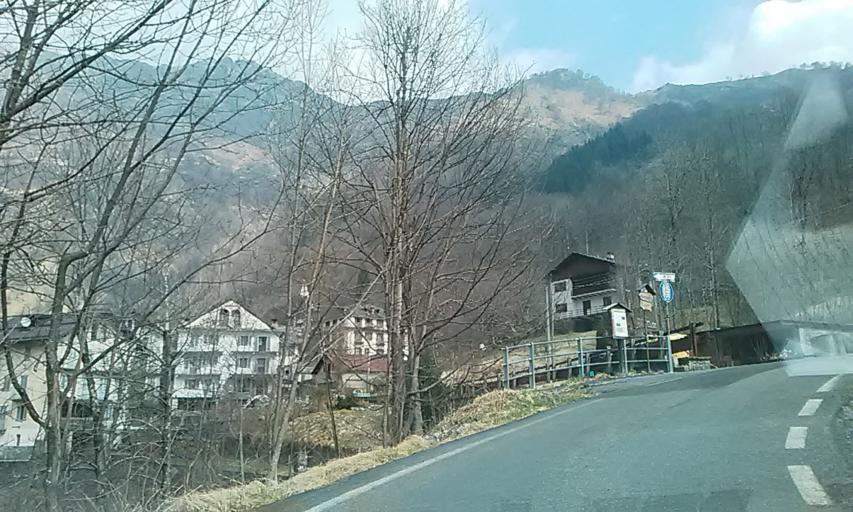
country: IT
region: Piedmont
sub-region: Provincia di Vercelli
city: Fobello
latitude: 45.8997
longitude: 8.1532
